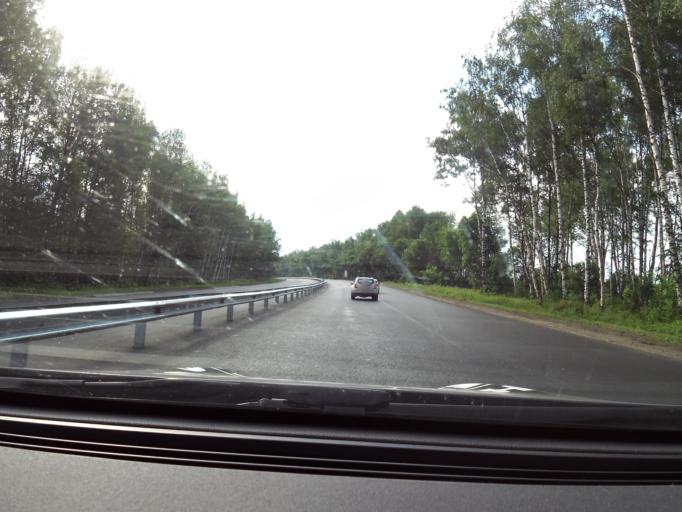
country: RU
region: Vladimir
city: Novovyazniki
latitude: 56.2014
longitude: 42.3561
